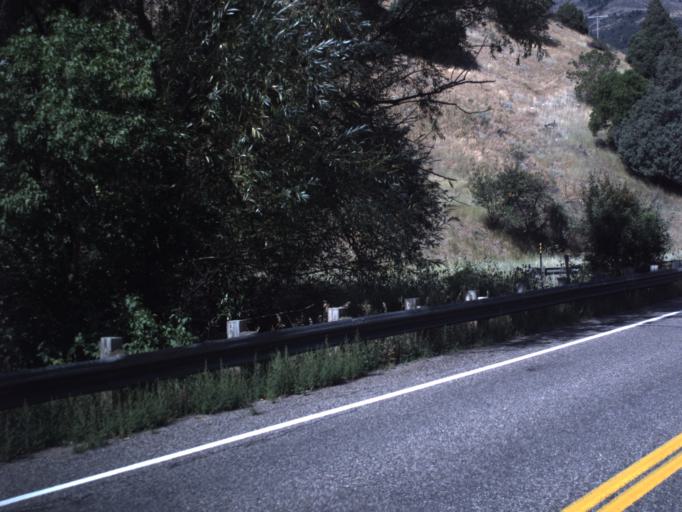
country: US
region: Utah
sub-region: Cache County
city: North Logan
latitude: 41.7564
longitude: -111.7123
